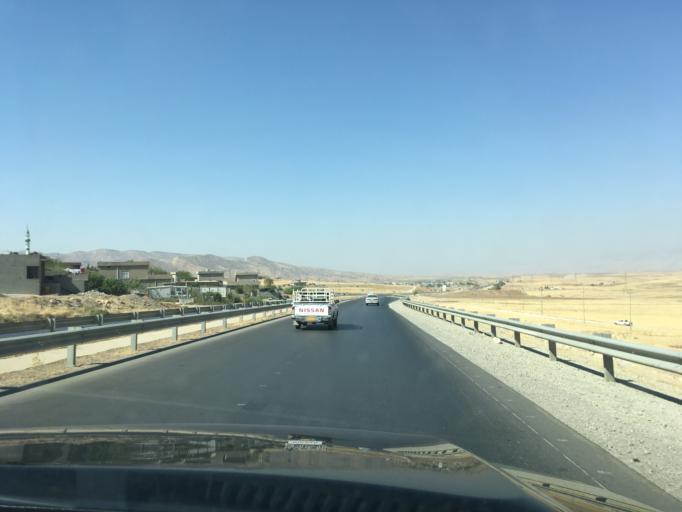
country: IQ
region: Arbil
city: Shaqlawah
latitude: 36.4917
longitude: 44.3734
